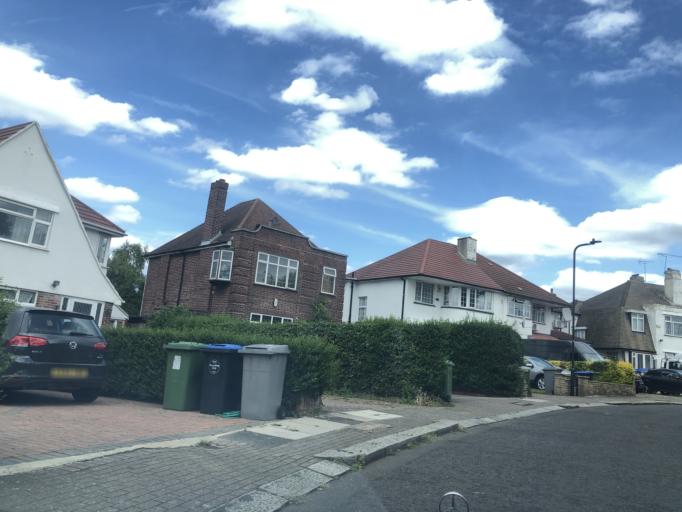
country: GB
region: England
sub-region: Greater London
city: Edgware
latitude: 51.5850
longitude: -0.2895
